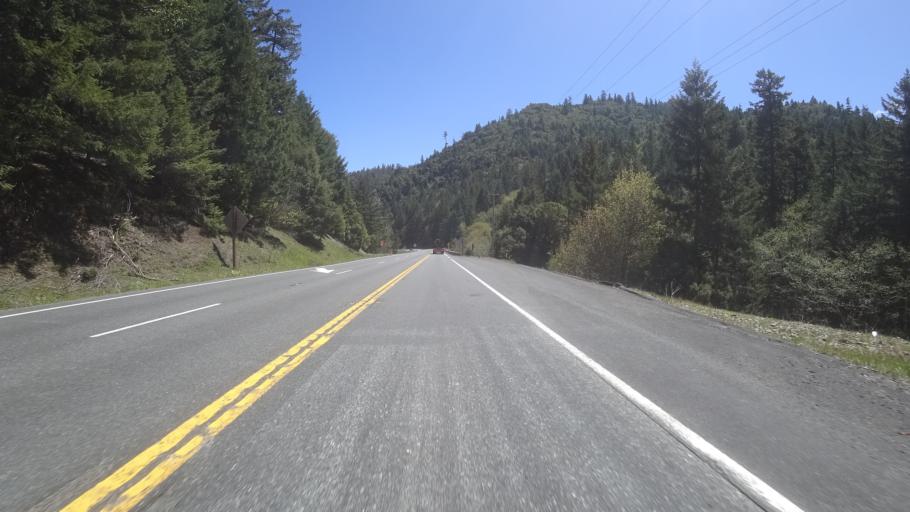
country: US
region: California
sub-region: Humboldt County
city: Willow Creek
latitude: 40.9053
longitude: -123.7457
